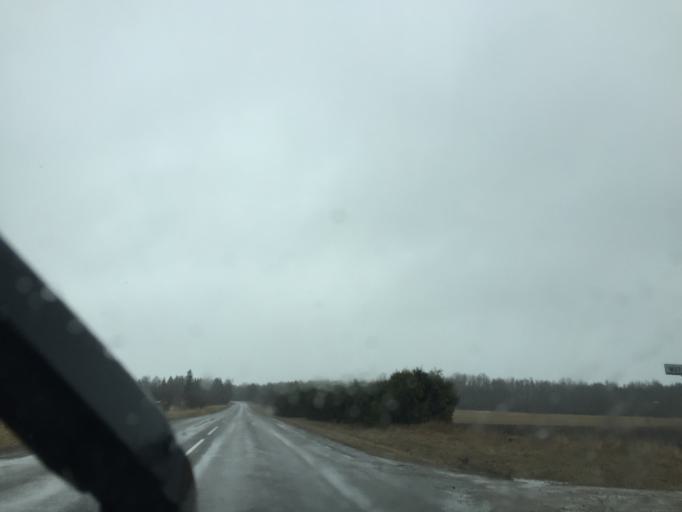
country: EE
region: Laeaene
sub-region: Ridala Parish
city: Uuemoisa
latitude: 58.8839
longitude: 23.6015
